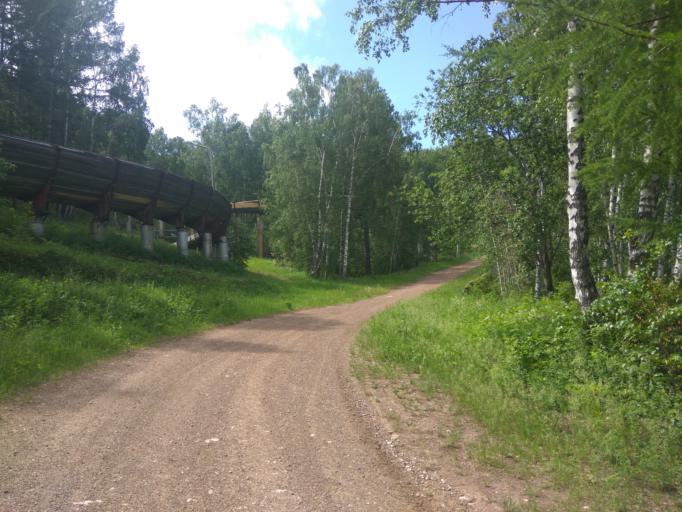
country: RU
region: Krasnoyarskiy
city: Krasnoyarsk
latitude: 55.9621
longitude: 92.8596
